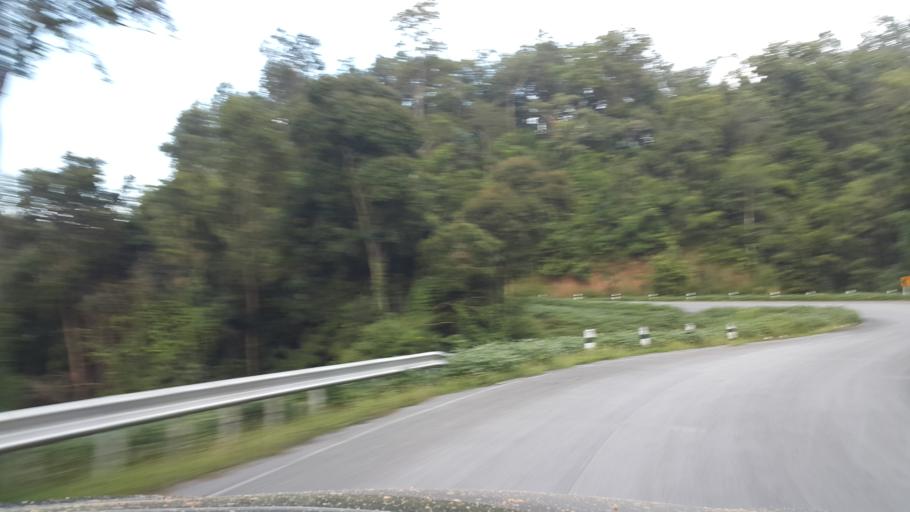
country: TH
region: Mae Hong Son
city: Mae Hi
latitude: 19.2456
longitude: 98.4592
